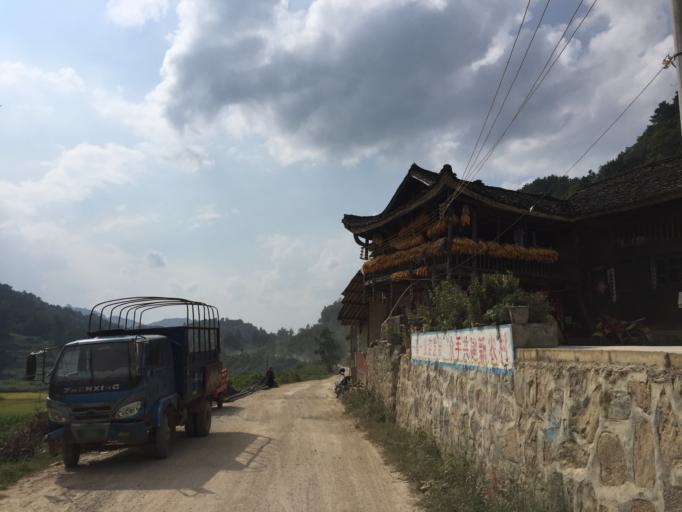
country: CN
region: Guizhou Sheng
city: Shiqian
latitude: 27.5906
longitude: 108.0069
